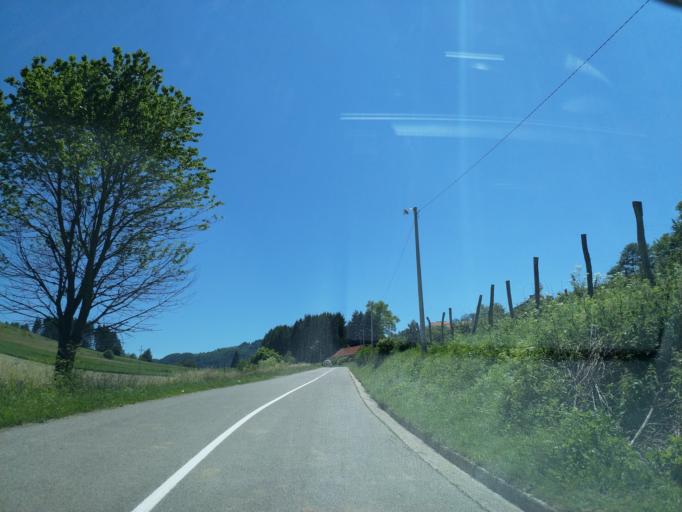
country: XK
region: Mitrovica
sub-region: Komuna e Leposaviqit
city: Leposaviq
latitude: 43.2814
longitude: 20.8751
